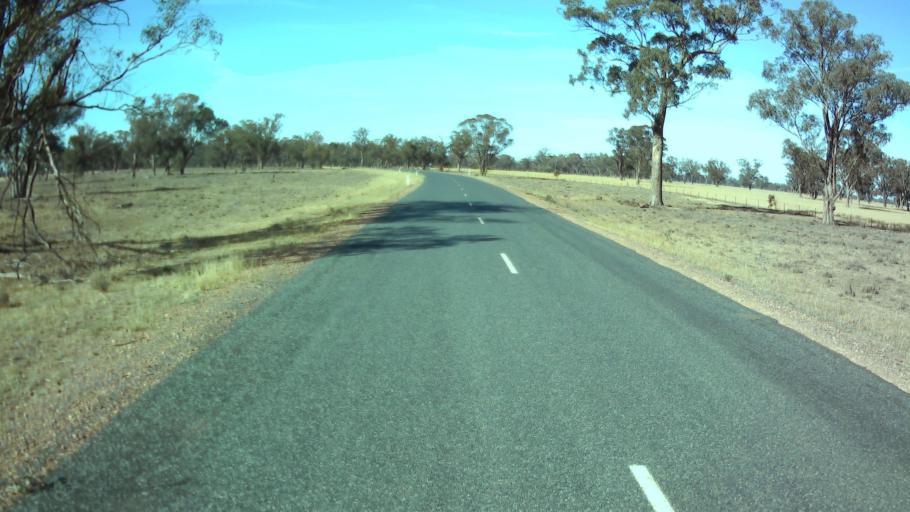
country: AU
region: New South Wales
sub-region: Weddin
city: Grenfell
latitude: -34.0577
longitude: 147.9124
